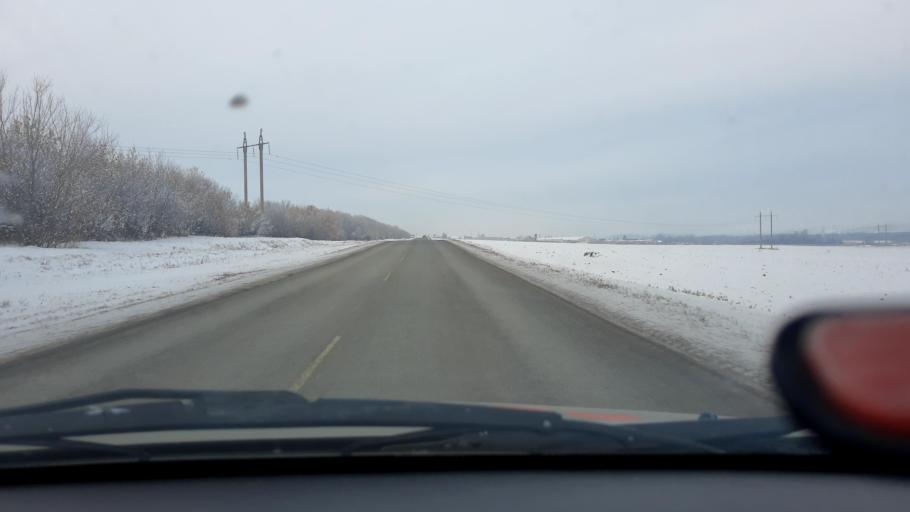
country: RU
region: Bashkortostan
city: Avdon
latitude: 54.4009
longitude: 55.8055
